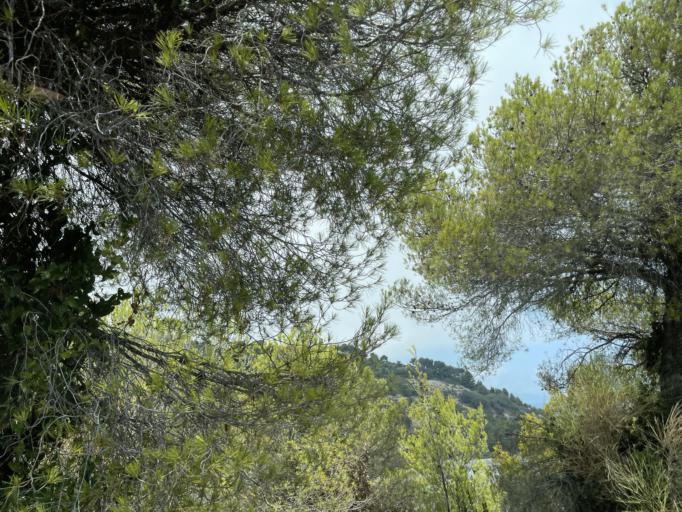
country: FR
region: Provence-Alpes-Cote d'Azur
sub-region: Departement des Alpes-Maritimes
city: Menton
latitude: 43.7866
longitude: 7.5462
